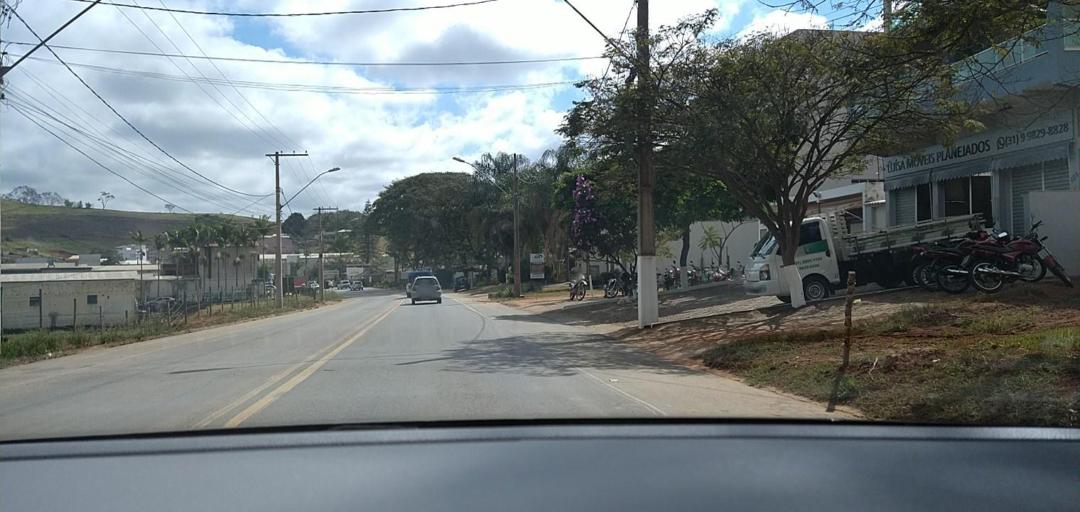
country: BR
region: Minas Gerais
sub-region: Vicosa
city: Vicosa
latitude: -20.6672
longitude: -42.8554
